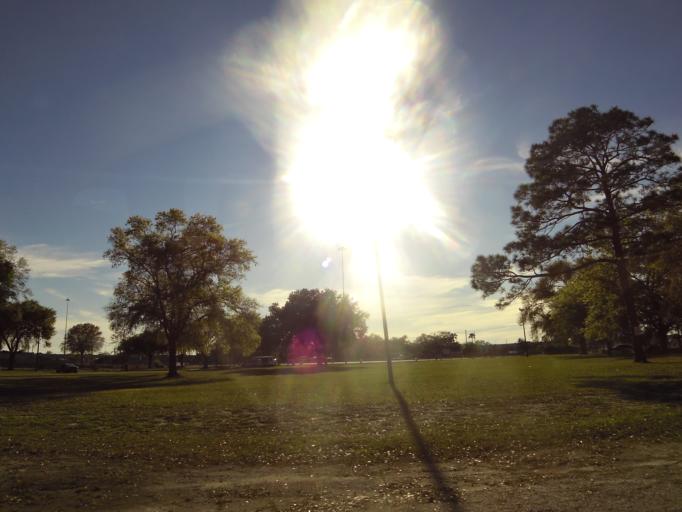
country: US
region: Florida
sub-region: Duval County
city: Jacksonville
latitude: 30.4605
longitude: -81.6333
